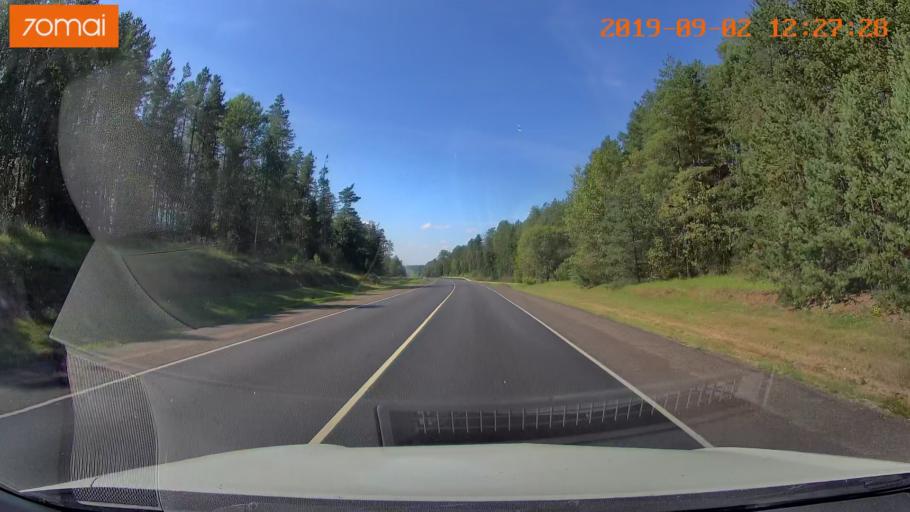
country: RU
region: Smolensk
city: Shumyachi
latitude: 53.8532
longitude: 32.5434
